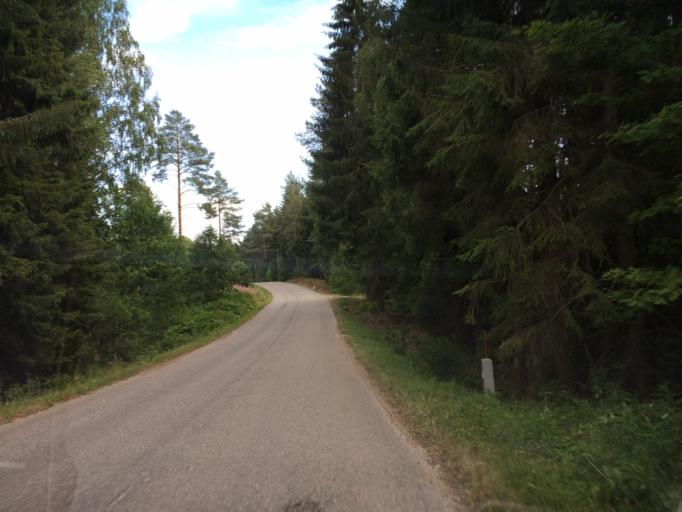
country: FI
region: Haeme
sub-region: Haemeenlinna
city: Hauho
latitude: 61.0761
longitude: 24.6641
